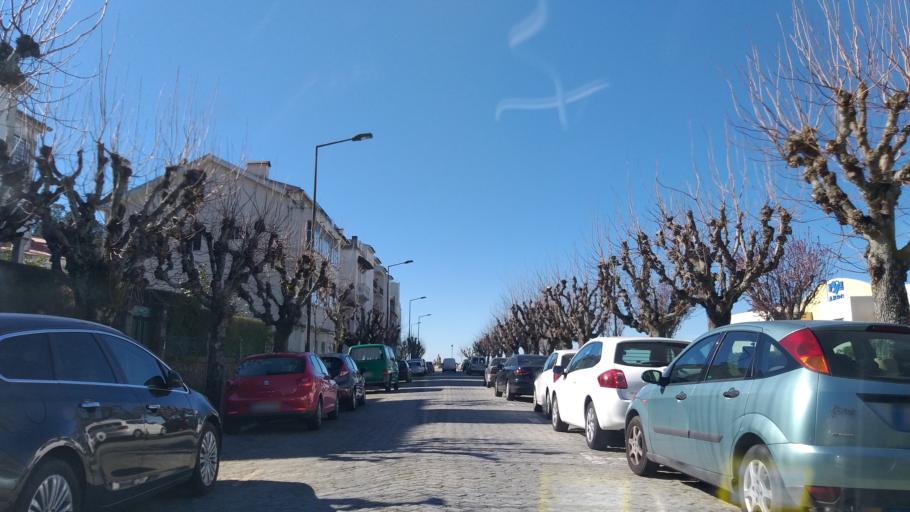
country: PT
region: Guarda
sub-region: Manteigas
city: Manteigas
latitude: 40.4923
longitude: -7.5965
